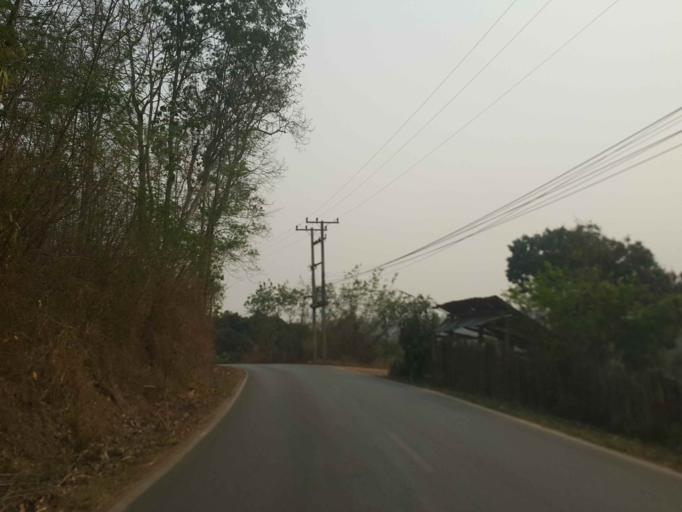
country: TH
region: Chiang Mai
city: Mae Taeng
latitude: 19.1055
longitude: 98.8987
